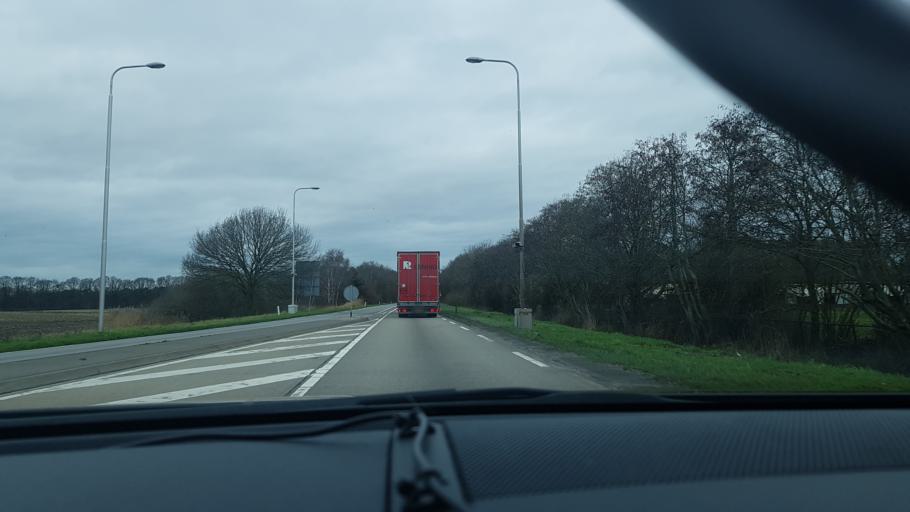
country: NL
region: North Brabant
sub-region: Gemeente Asten
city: Asten
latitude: 51.4552
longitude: 5.7211
